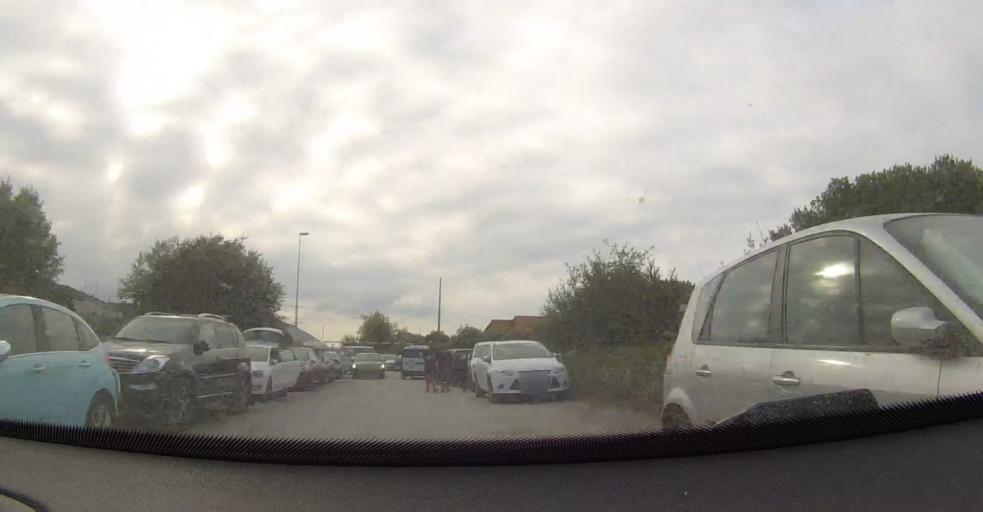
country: ES
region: Cantabria
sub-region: Provincia de Cantabria
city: Argonos
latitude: 43.4722
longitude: -3.5040
